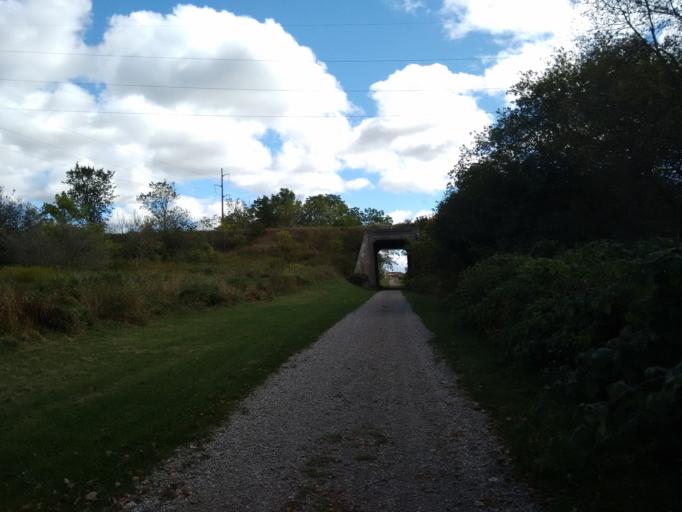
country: CA
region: Ontario
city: Stratford
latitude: 43.2474
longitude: -81.1410
